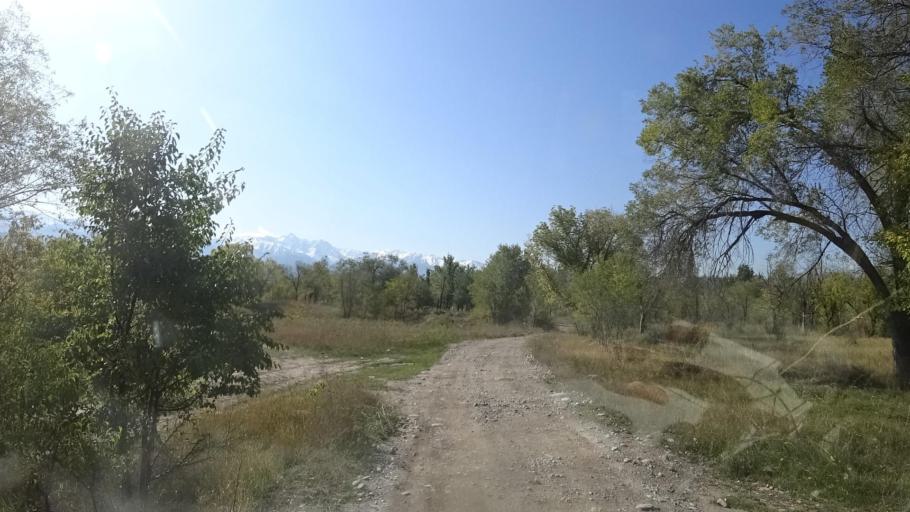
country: KZ
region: Almaty Oblysy
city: Pervomayskiy
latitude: 43.3341
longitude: 76.9995
